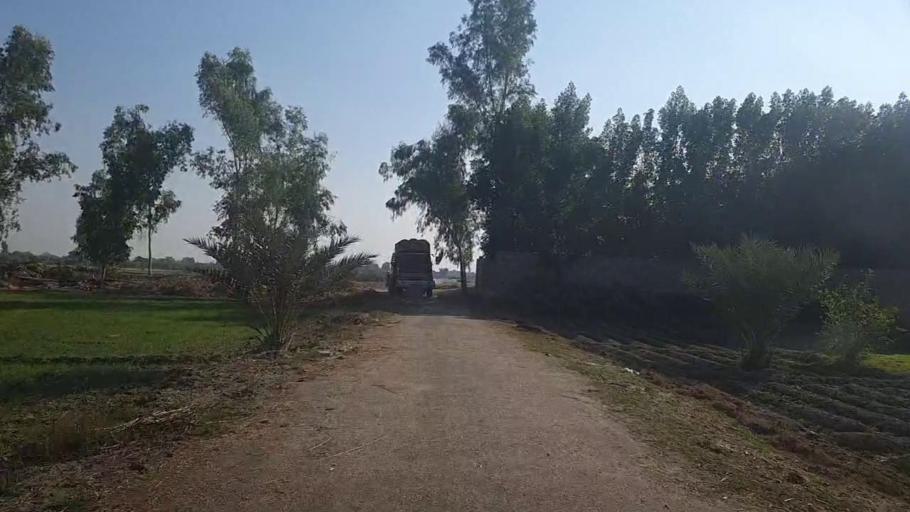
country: PK
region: Sindh
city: Kot Diji
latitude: 27.4317
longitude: 68.7317
